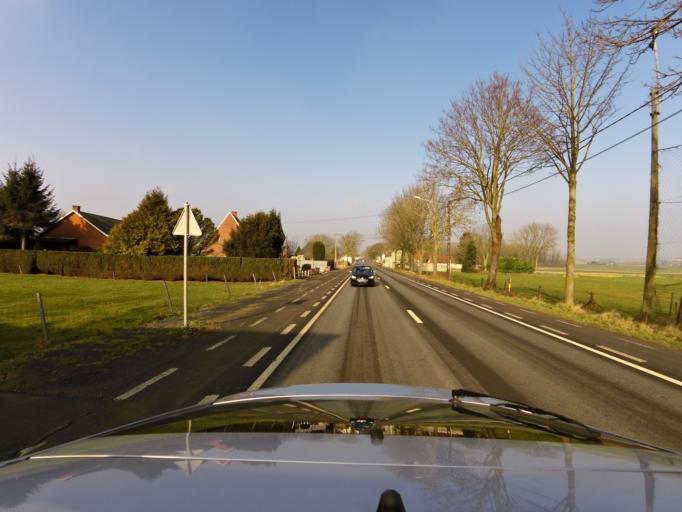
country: BE
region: Wallonia
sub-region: Province du Hainaut
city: Peruwelz
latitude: 50.5722
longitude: 3.5644
